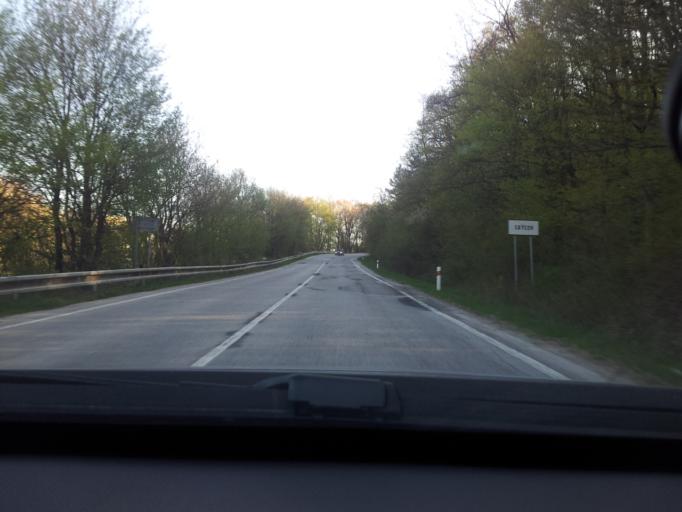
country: SK
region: Nitriansky
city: Zlate Moravce
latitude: 48.4967
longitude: 18.4232
